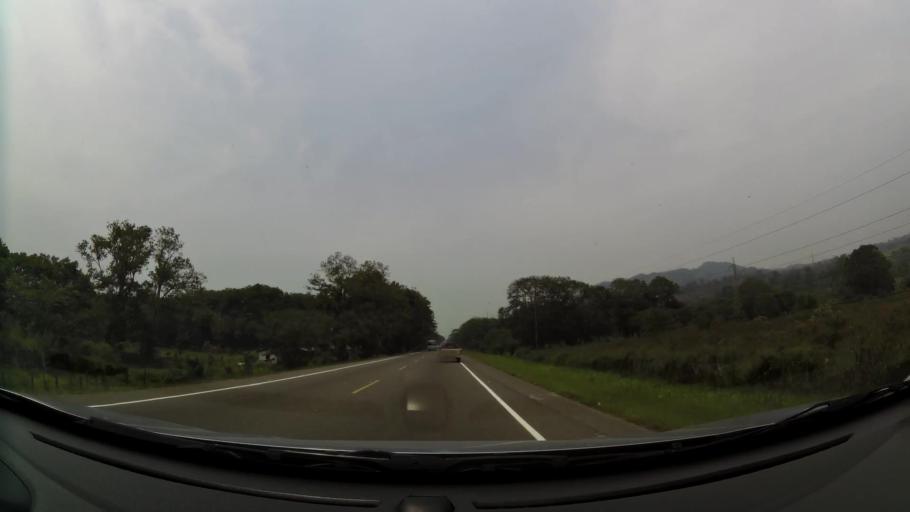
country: HN
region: Cortes
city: La Guama
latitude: 14.8243
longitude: -87.9614
